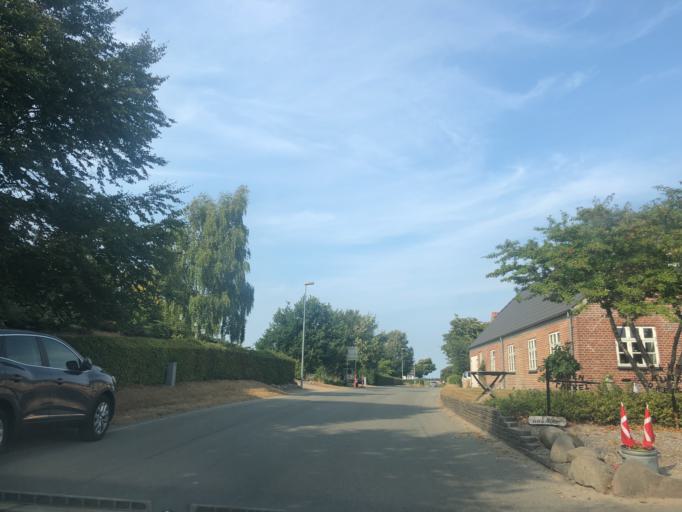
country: DK
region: North Denmark
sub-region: Morso Kommune
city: Nykobing Mors
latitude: 56.8187
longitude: 9.0288
